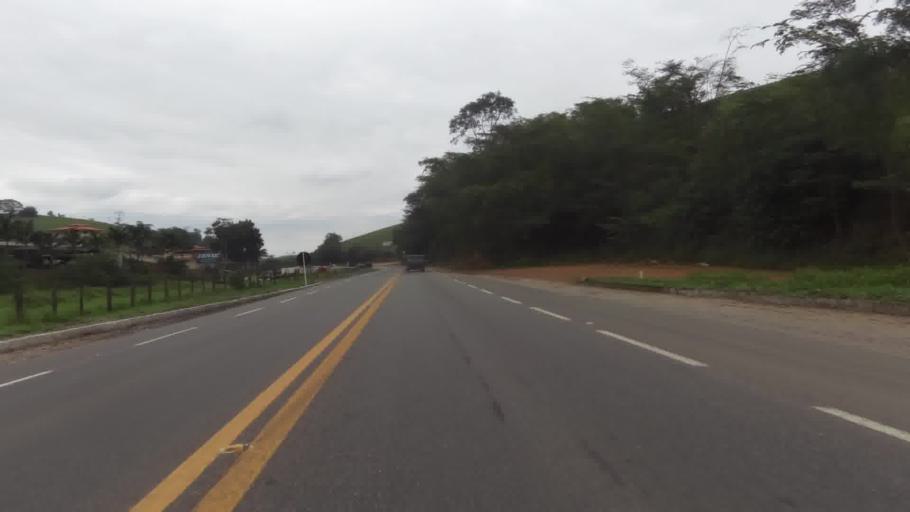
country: BR
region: Espirito Santo
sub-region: Iconha
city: Iconha
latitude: -20.7764
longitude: -40.7788
